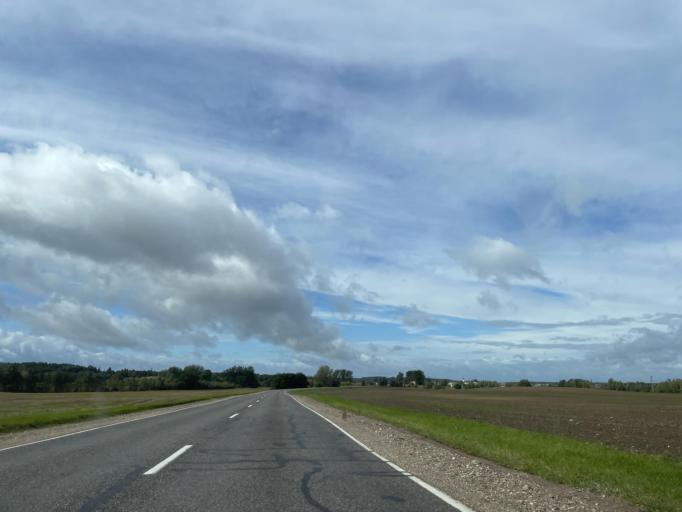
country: BY
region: Brest
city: Kosava
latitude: 52.7441
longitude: 25.1853
